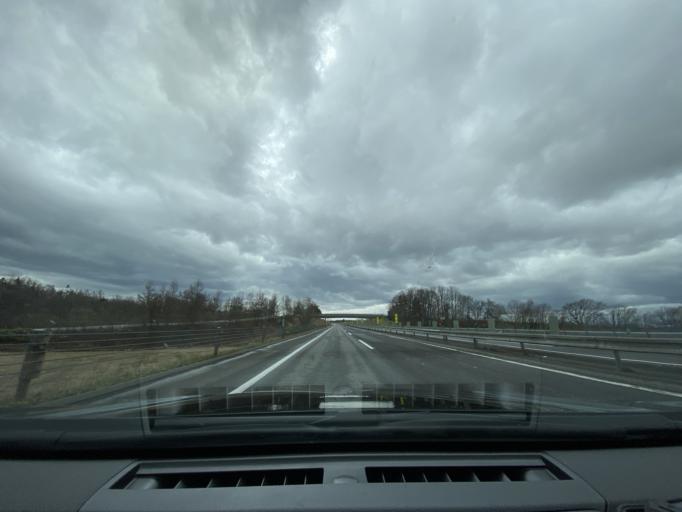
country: JP
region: Hokkaido
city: Fukagawa
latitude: 43.6294
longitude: 141.9817
